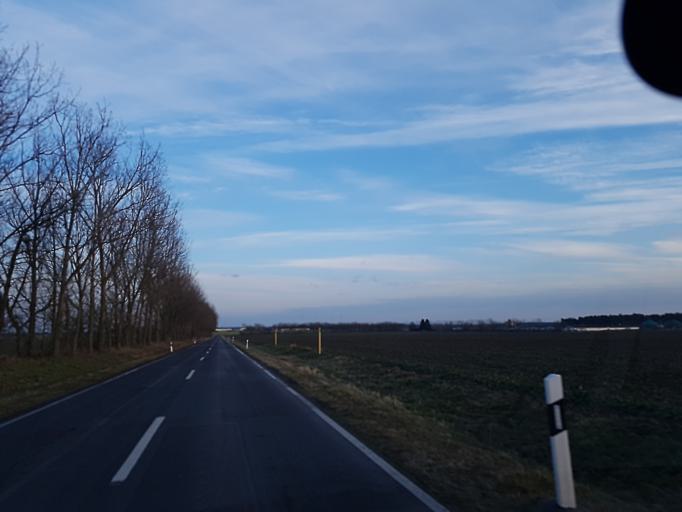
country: DE
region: Brandenburg
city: Juterbog
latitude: 51.9238
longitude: 13.0641
